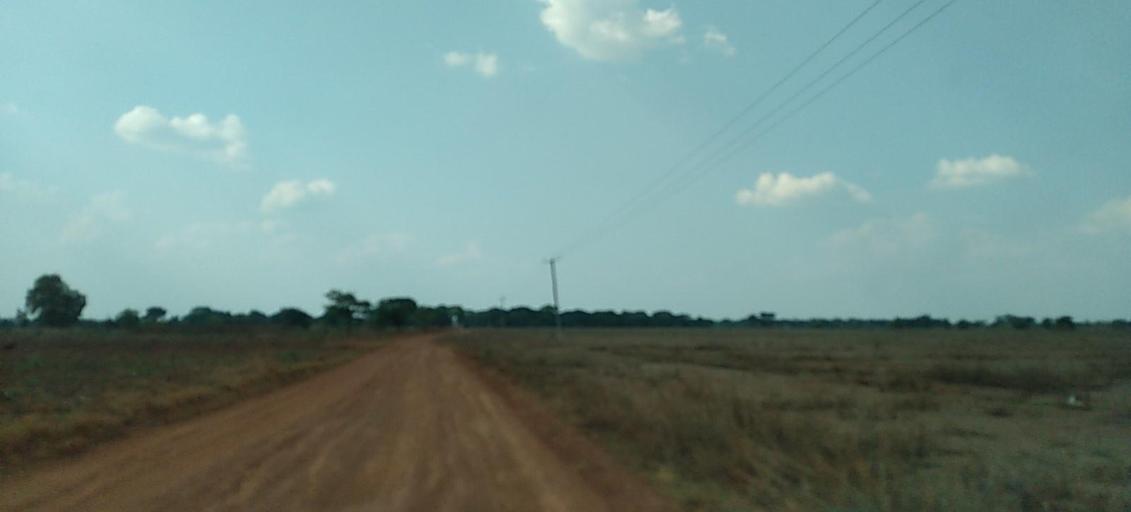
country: ZM
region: Copperbelt
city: Mpongwe
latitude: -13.5199
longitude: 28.0990
